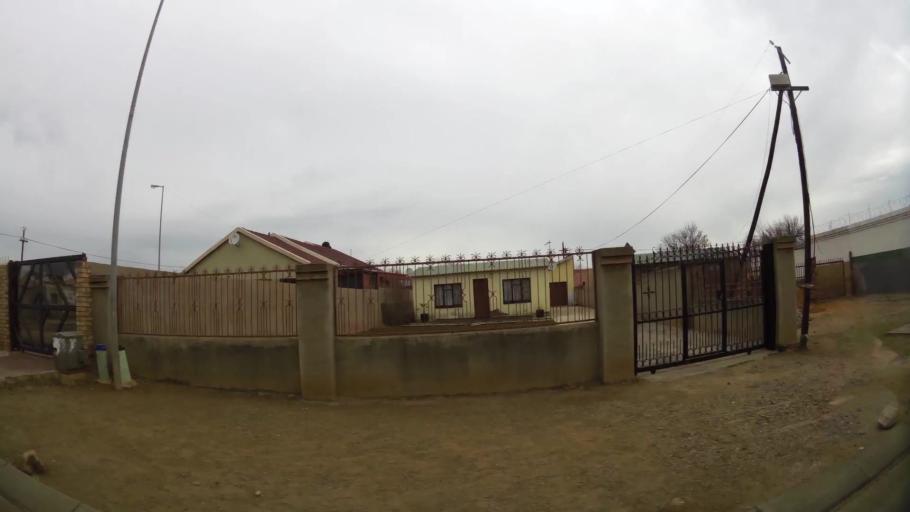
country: ZA
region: Gauteng
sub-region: City of Tshwane Metropolitan Municipality
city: Pretoria
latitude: -25.7071
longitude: 28.3548
